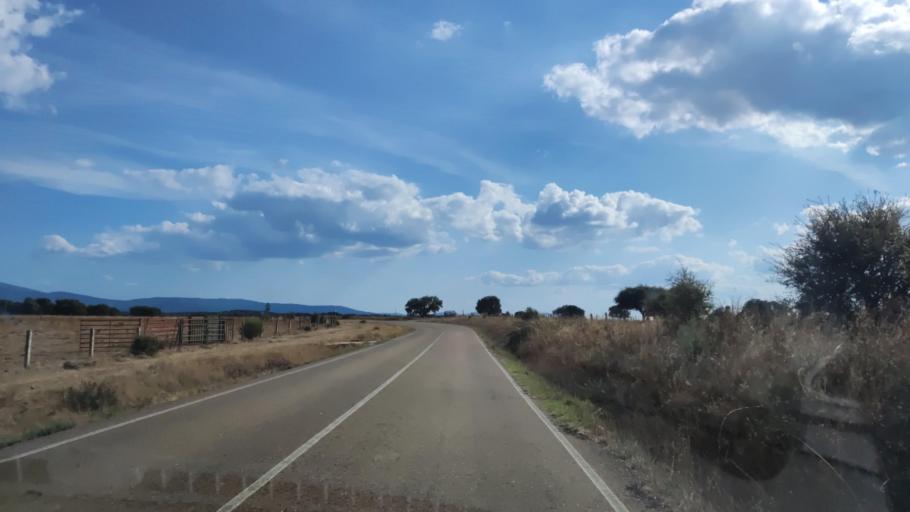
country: ES
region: Castille and Leon
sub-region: Provincia de Salamanca
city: Martiago
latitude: 40.4858
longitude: -6.4937
